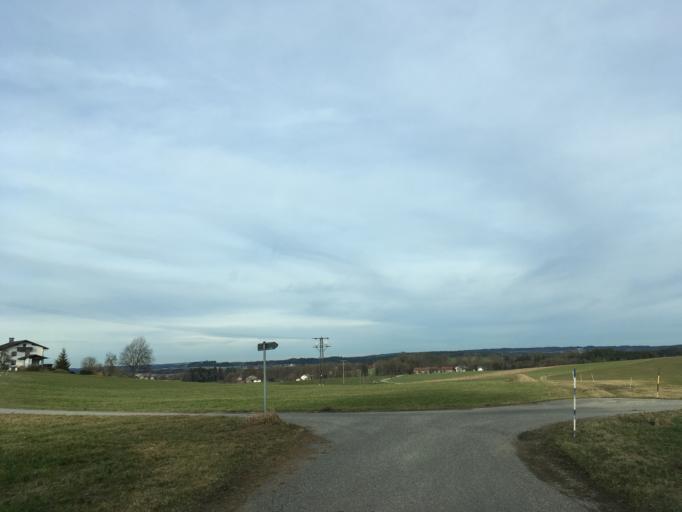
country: DE
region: Bavaria
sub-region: Upper Bavaria
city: Sochtenau
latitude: 47.9402
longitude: 12.2062
